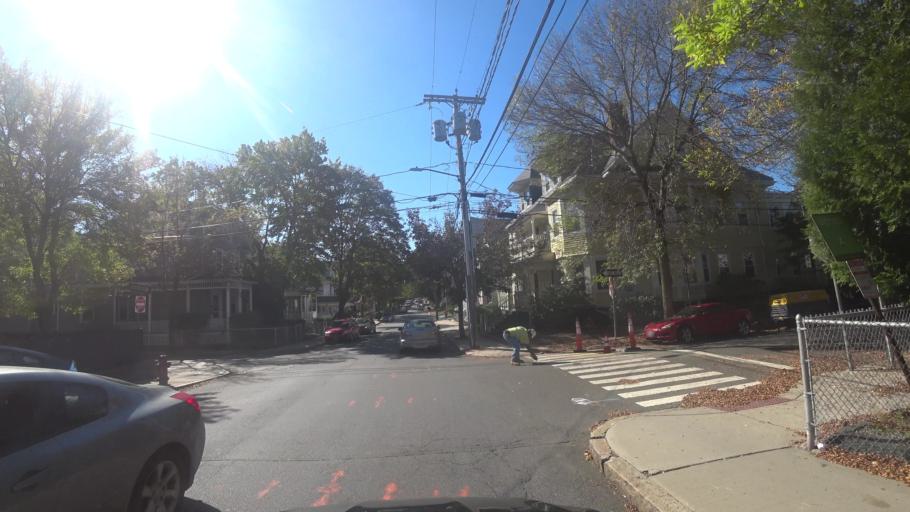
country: US
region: Massachusetts
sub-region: Middlesex County
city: Somerville
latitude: 42.3882
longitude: -71.1037
